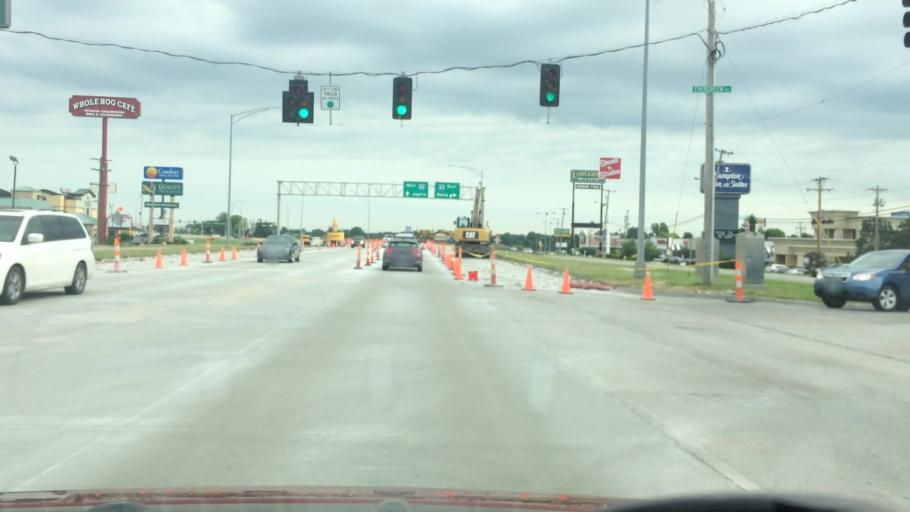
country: US
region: Missouri
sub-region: Greene County
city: Springfield
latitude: 37.2456
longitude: -93.2608
